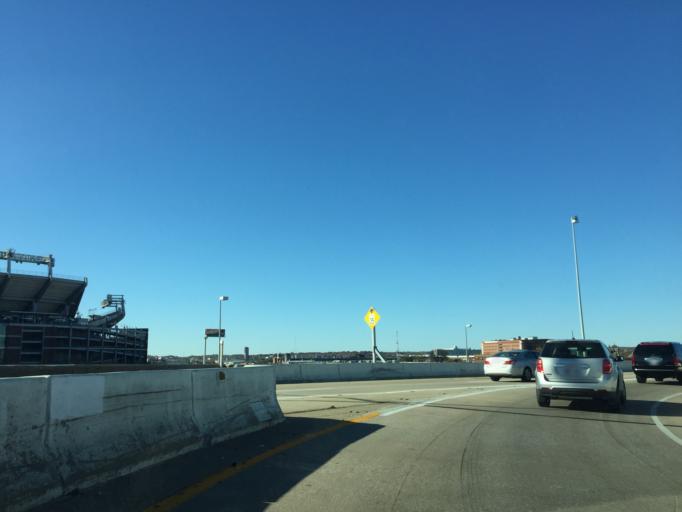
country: US
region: Maryland
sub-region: City of Baltimore
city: Baltimore
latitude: 39.2809
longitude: -76.6212
